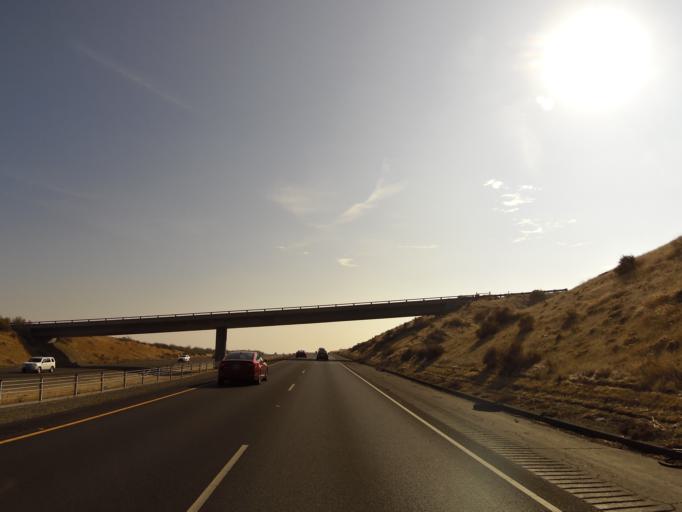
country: US
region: California
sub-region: Kings County
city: Avenal
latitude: 36.0541
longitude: -120.0647
